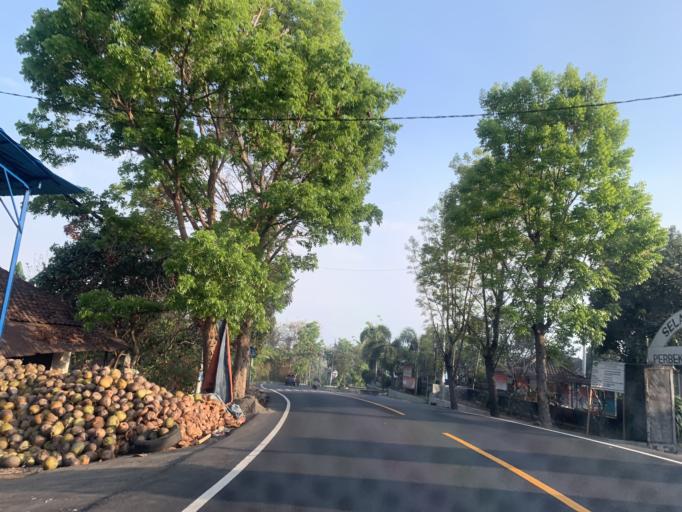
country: ID
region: Bali
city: Banjar Delodrurung
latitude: -8.5018
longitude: 115.0181
